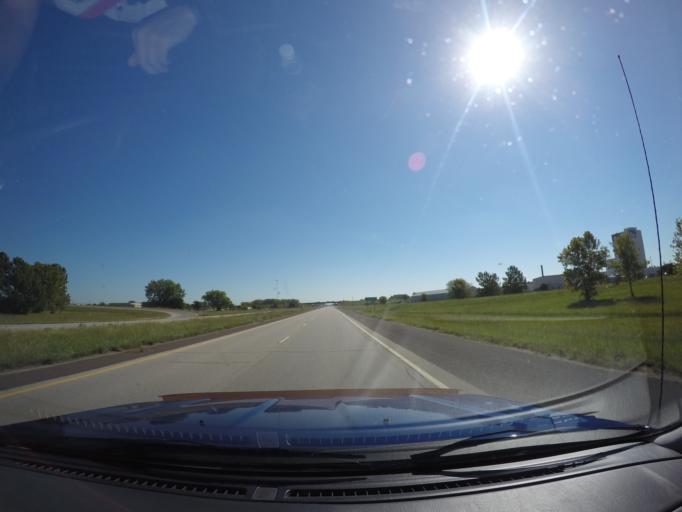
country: US
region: Kansas
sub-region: Shawnee County
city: Topeka
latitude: 39.0905
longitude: -95.7253
